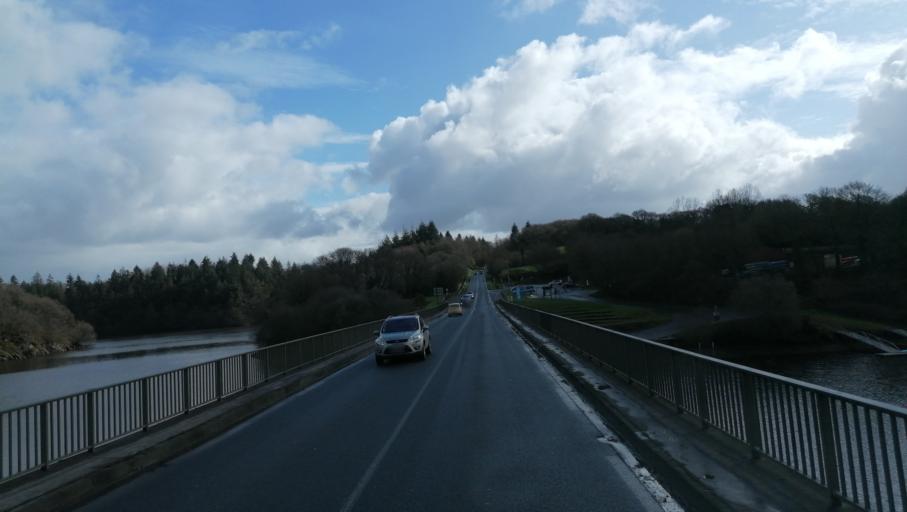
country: FR
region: Brittany
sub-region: Departement des Cotes-d'Armor
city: La Meaugon
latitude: 48.4903
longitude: -2.8437
